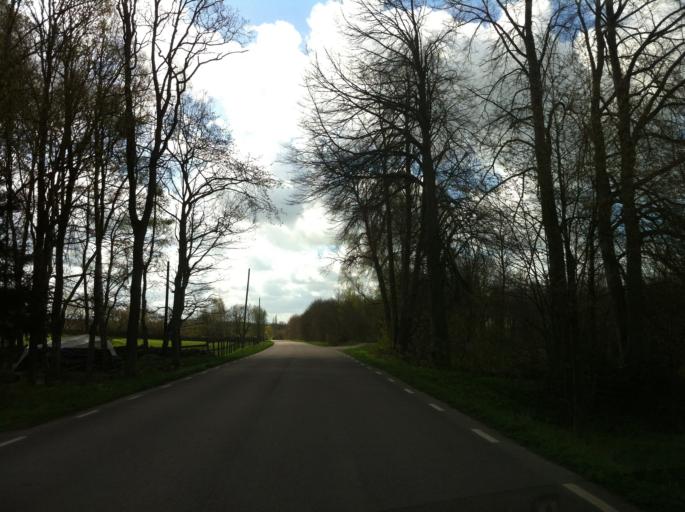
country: SE
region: Skane
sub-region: Horby Kommun
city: Hoerby
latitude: 55.8864
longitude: 13.6172
